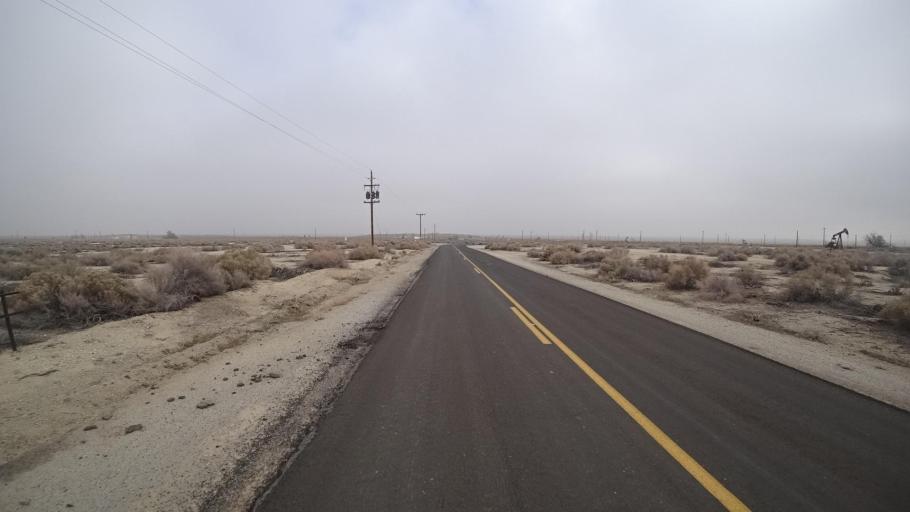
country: US
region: California
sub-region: Kern County
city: Maricopa
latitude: 35.0772
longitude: -119.3707
